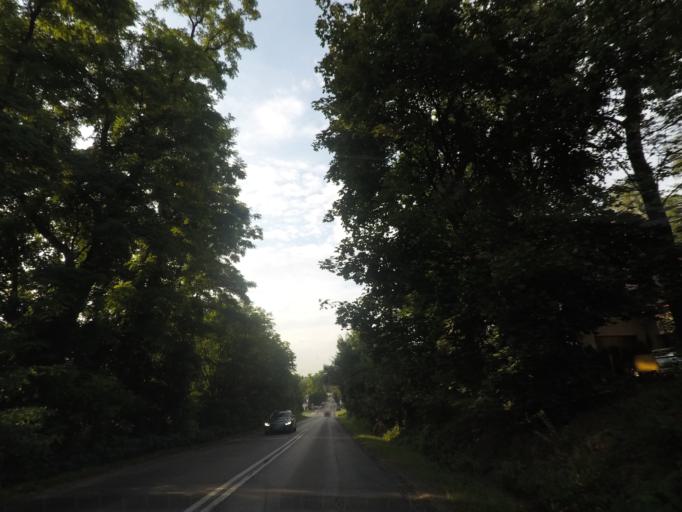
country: PL
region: Lesser Poland Voivodeship
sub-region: Powiat wielicki
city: Wieliczka
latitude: 49.9899
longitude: 20.0419
